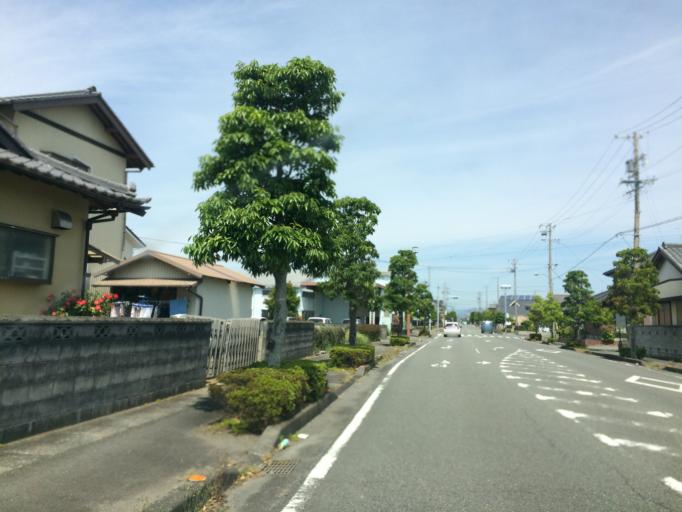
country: JP
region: Shizuoka
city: Sagara
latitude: 34.7543
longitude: 138.2542
